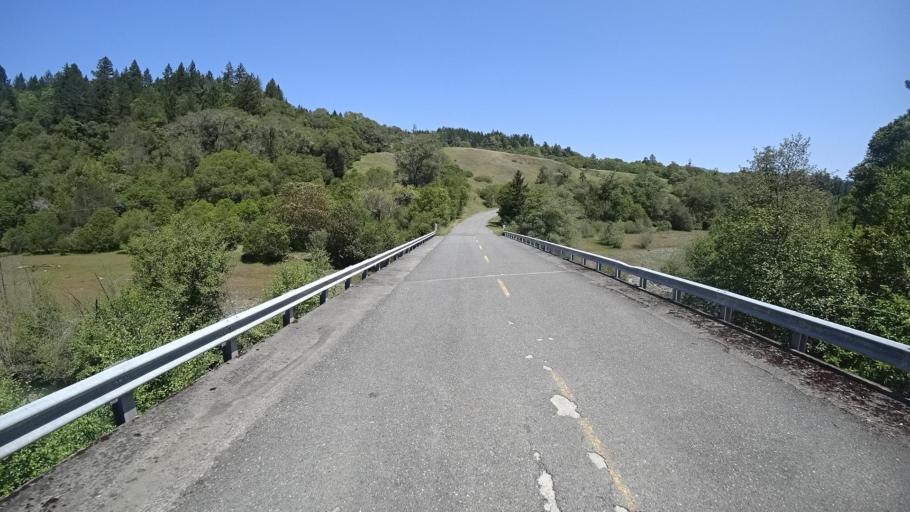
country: US
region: California
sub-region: Humboldt County
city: Redway
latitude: 40.2366
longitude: -123.6358
